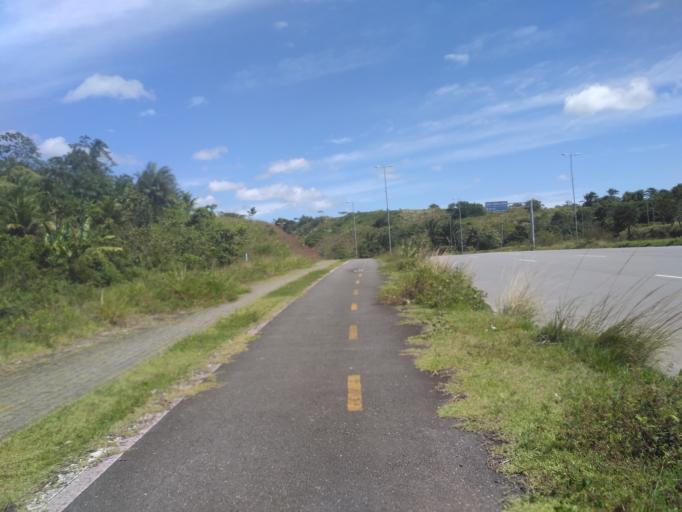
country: BR
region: Pernambuco
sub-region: Sao Lourenco Da Mata
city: Sao Lourenco da Mata
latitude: -8.0426
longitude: -34.9960
